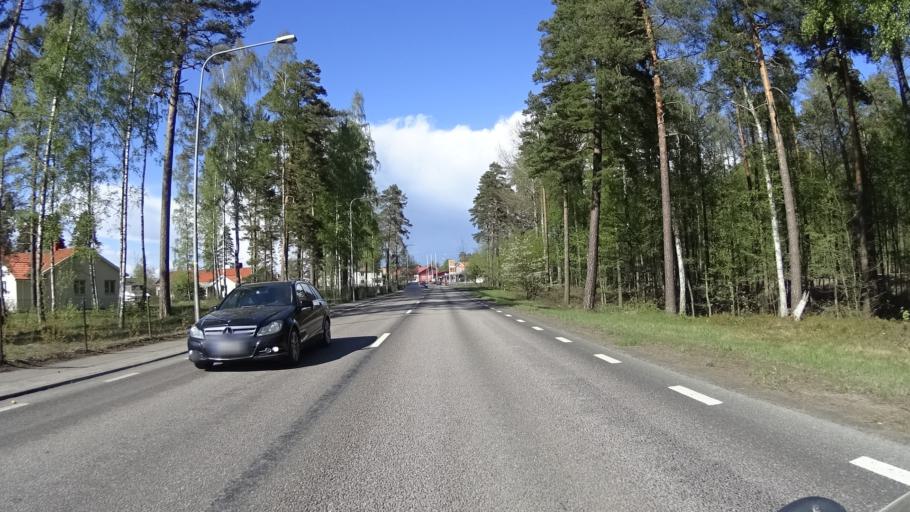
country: SE
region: Vaestra Goetaland
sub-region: Karlsborgs Kommun
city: Karlsborg
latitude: 58.5242
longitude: 14.5104
